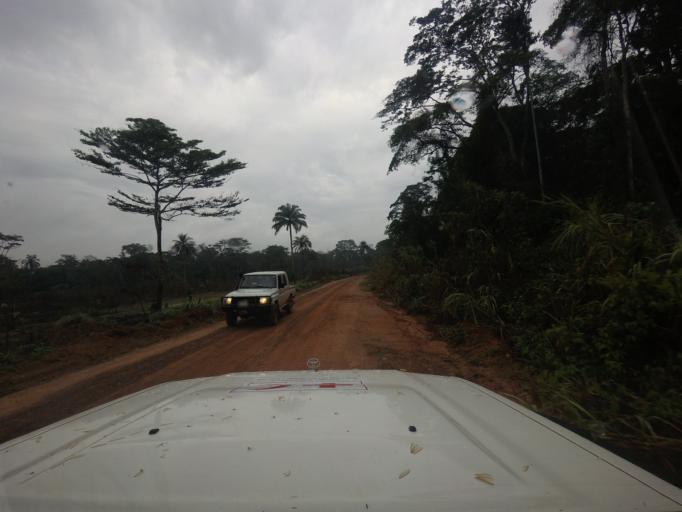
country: LR
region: Lofa
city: Voinjama
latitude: 8.3887
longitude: -9.8144
